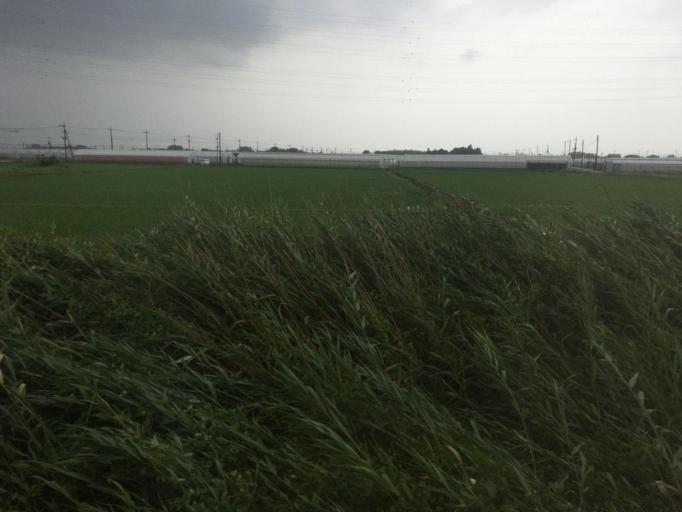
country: JP
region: Tochigi
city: Ashikaga
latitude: 36.2920
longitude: 139.4703
